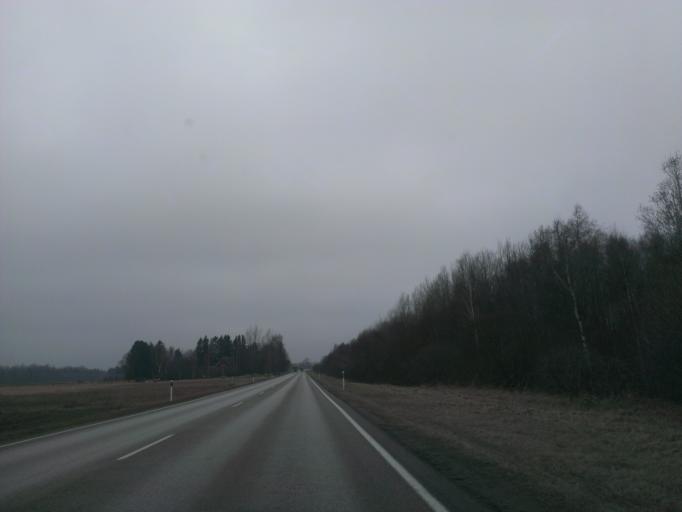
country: EE
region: Paernumaa
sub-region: Audru vald
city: Audru
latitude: 58.4394
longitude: 24.2509
